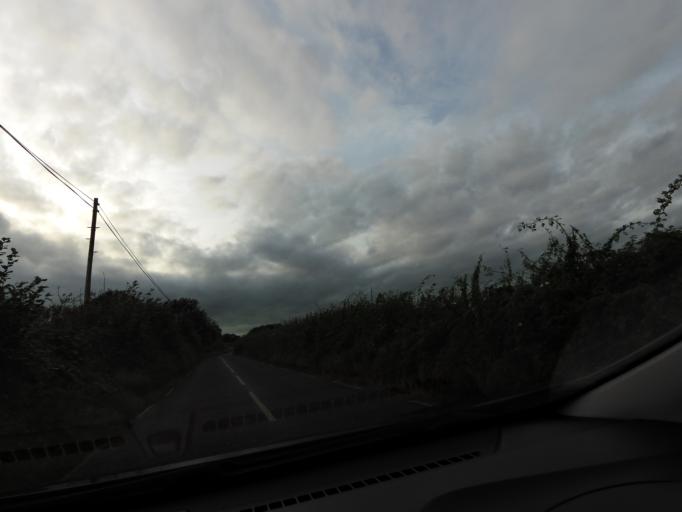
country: IE
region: Leinster
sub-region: Uibh Fhaili
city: Ferbane
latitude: 53.1864
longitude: -7.7466
